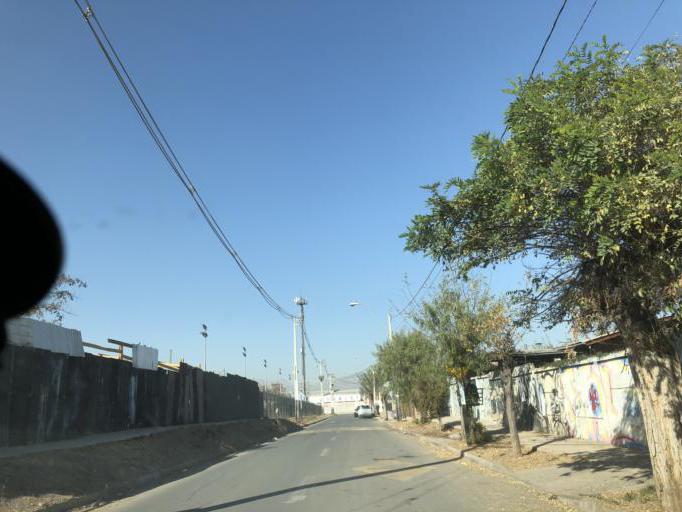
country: CL
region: Santiago Metropolitan
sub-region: Provincia de Santiago
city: La Pintana
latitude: -33.6165
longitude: -70.6227
